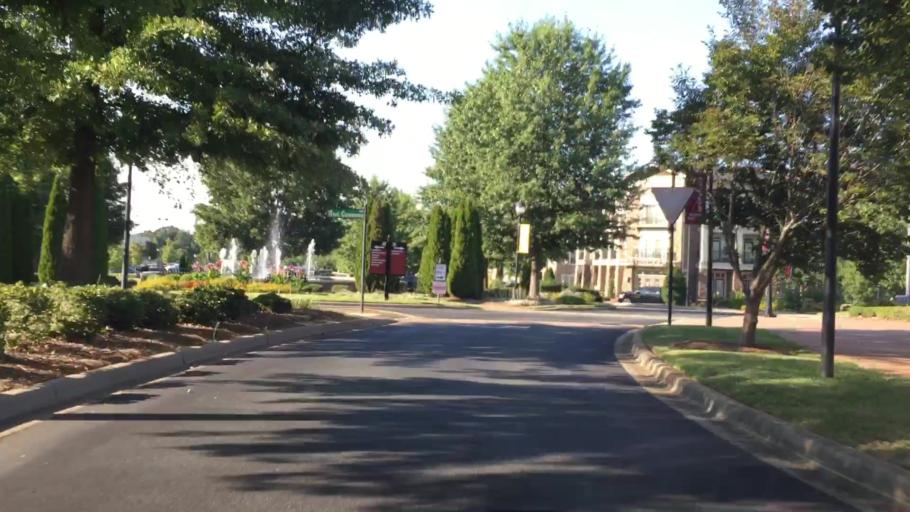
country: US
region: North Carolina
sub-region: Iredell County
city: Mooresville
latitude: 35.5855
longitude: -80.8710
